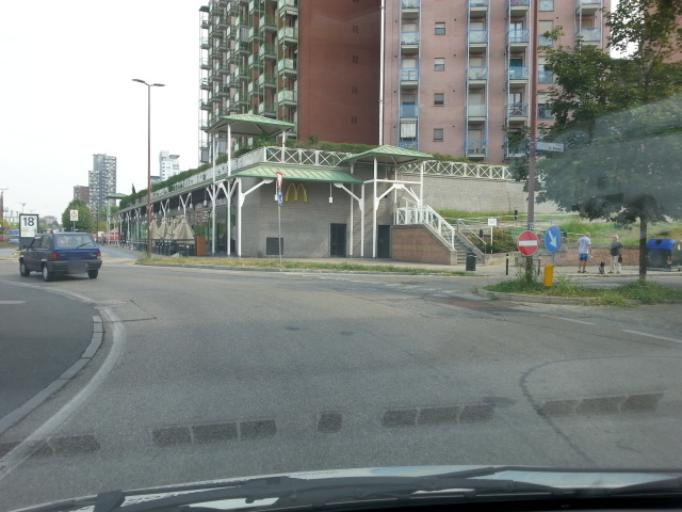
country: IT
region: Piedmont
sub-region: Provincia di Torino
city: Turin
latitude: 45.0866
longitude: 7.6697
